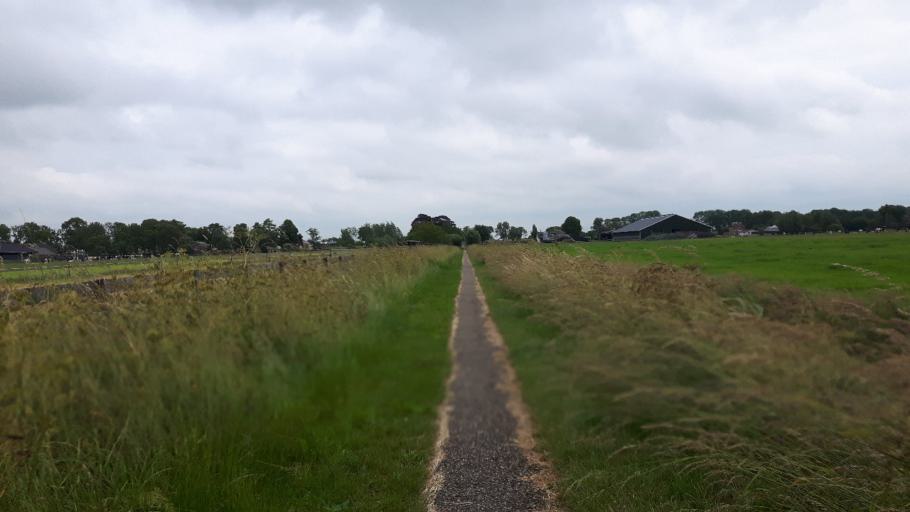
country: NL
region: Utrecht
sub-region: Gemeente Oudewater
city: Oudewater
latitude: 52.0256
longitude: 4.8547
